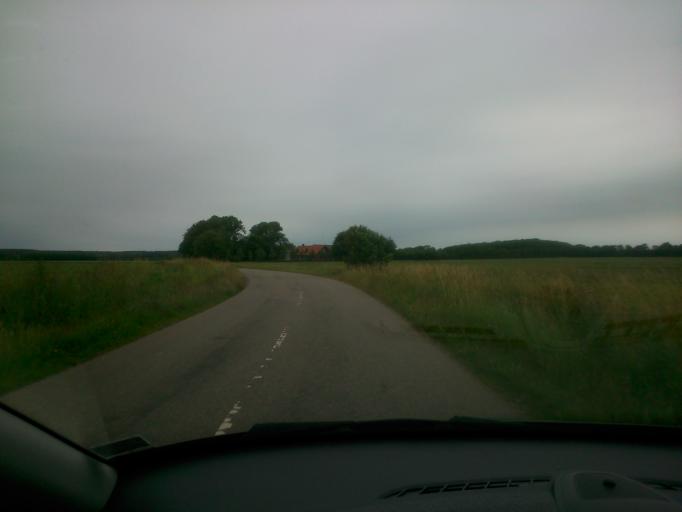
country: DK
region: Central Jutland
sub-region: Ringkobing-Skjern Kommune
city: Skjern
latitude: 56.0062
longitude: 8.4998
